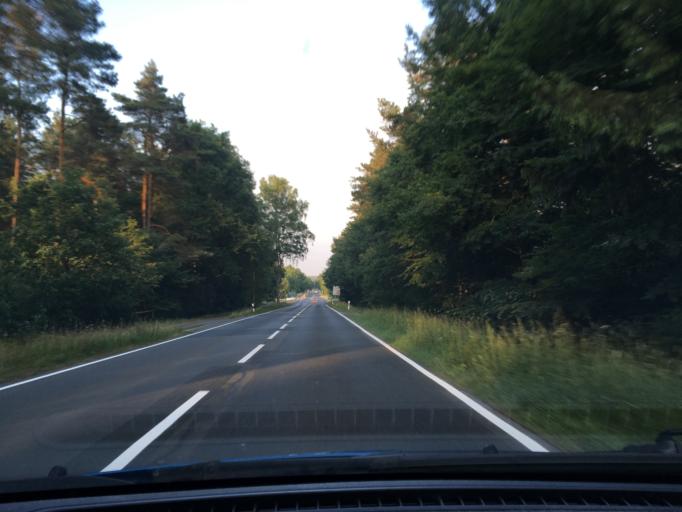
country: DE
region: Lower Saxony
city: Garlstorf
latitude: 53.2377
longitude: 10.0723
